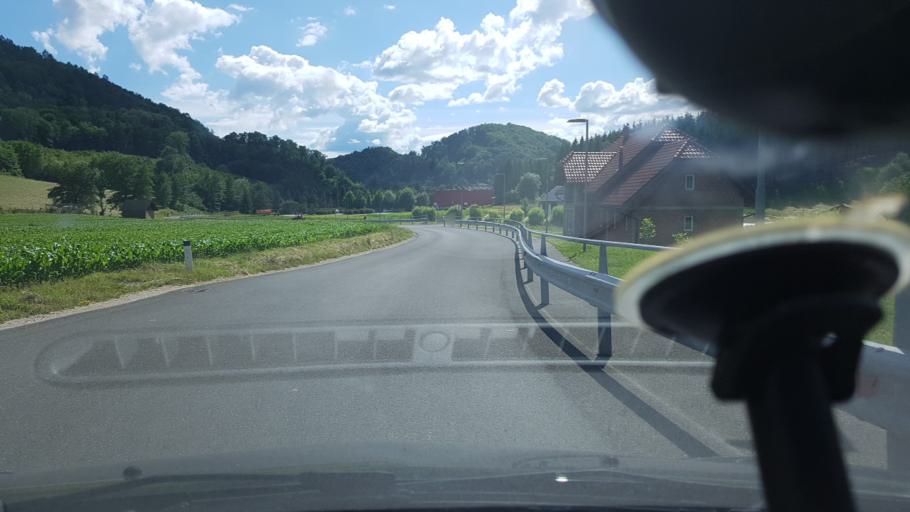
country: SI
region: Rogatec
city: Rogatec
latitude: 46.2375
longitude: 15.7096
